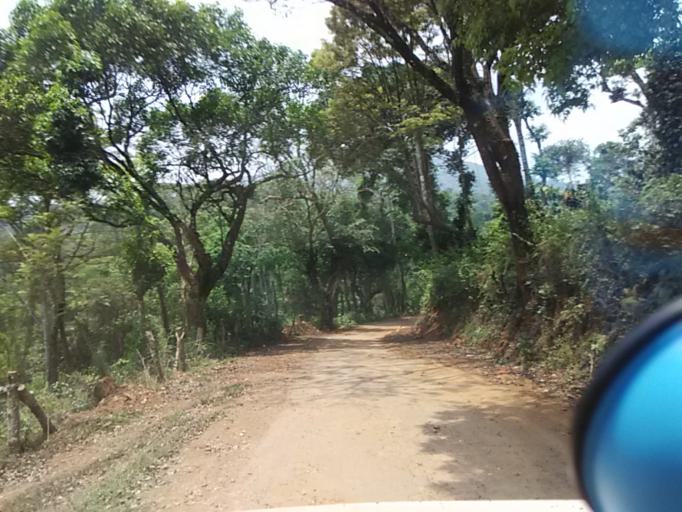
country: IN
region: Karnataka
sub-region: Kodagu
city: Virarajendrapet
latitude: 12.2149
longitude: 75.6812
